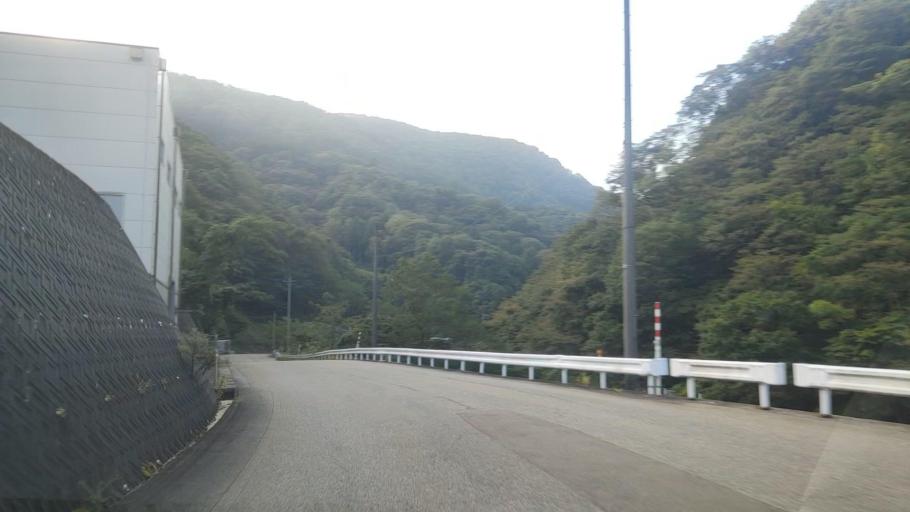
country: JP
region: Toyama
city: Yatsuomachi-higashikumisaka
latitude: 36.4859
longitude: 137.0667
